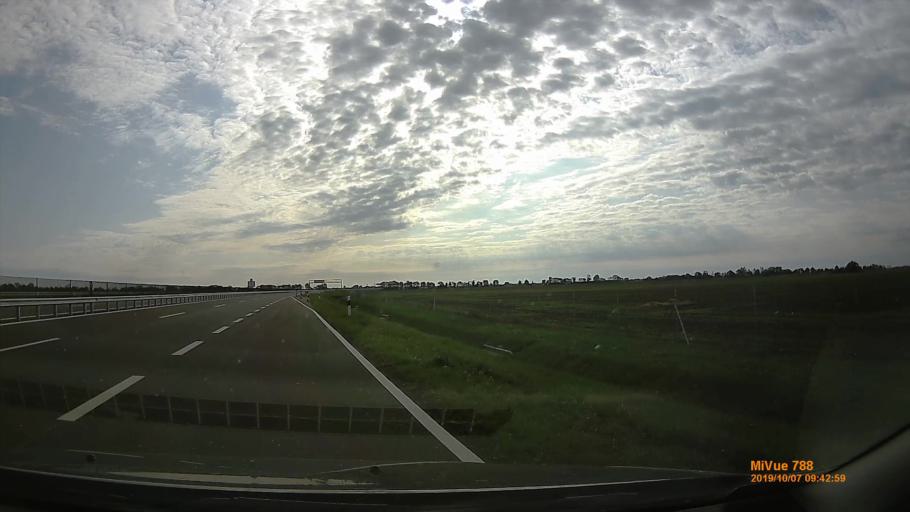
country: HU
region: Bekes
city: Kondoros
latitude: 46.8109
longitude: 20.6804
